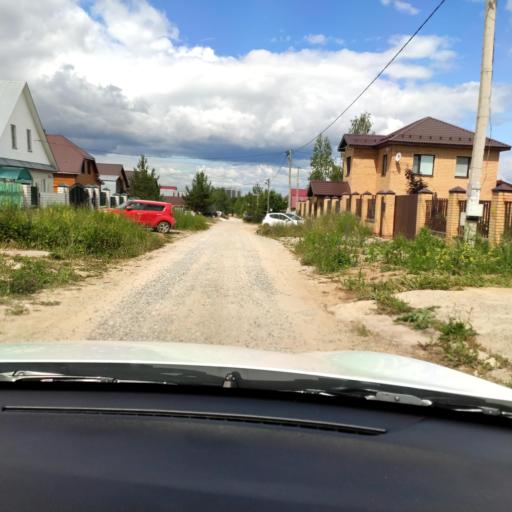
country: RU
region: Tatarstan
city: Vysokaya Gora
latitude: 55.7828
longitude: 49.2718
